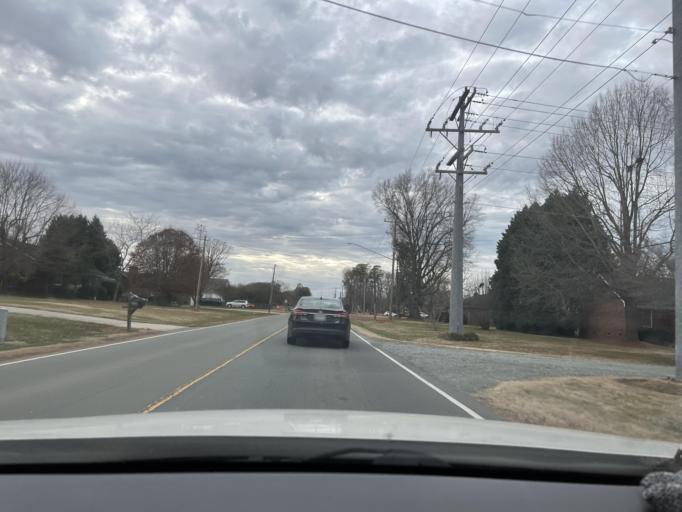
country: US
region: North Carolina
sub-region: Alamance County
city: Elon
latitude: 36.0724
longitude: -79.5057
